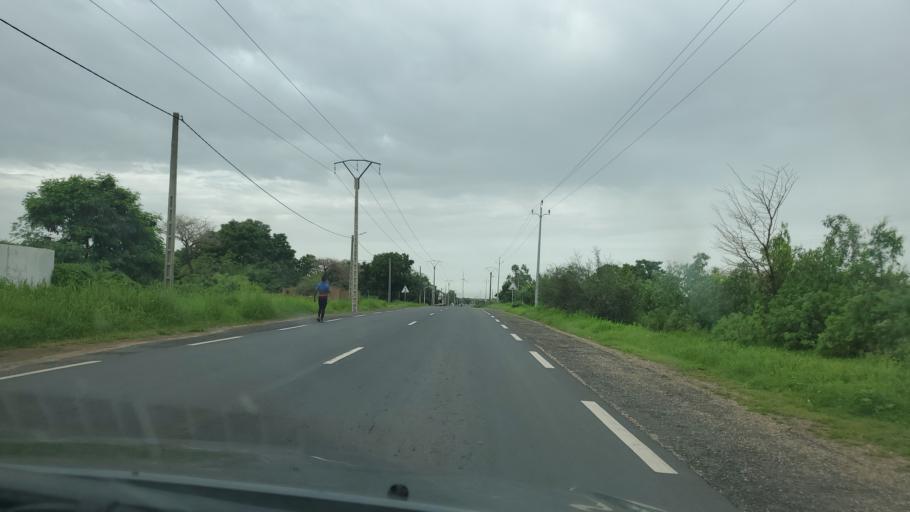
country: SN
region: Thies
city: Kayar
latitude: 15.1019
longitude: -16.9135
